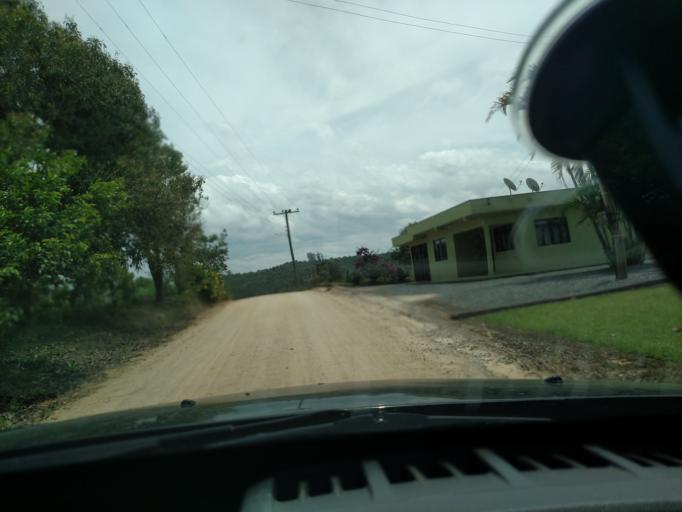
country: BR
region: Santa Catarina
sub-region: Gaspar
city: Gaspar
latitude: -26.9468
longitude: -48.8109
